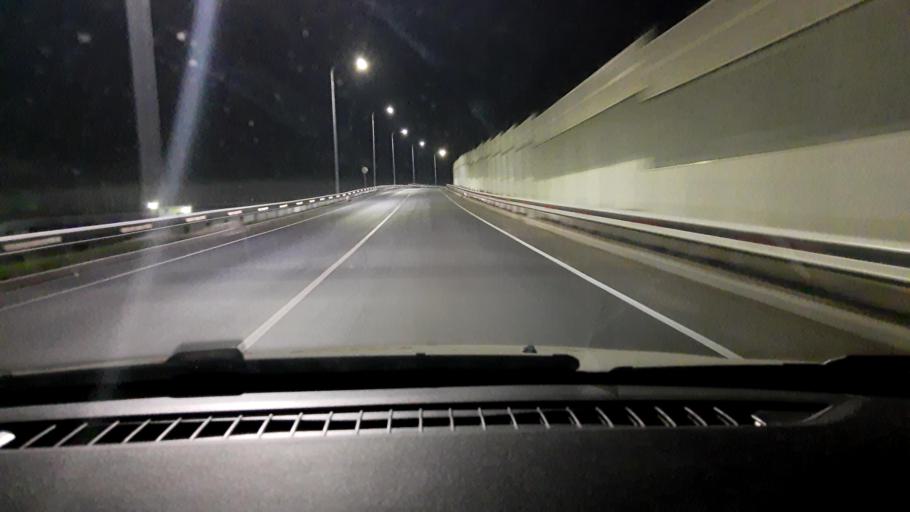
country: RU
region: Nizjnij Novgorod
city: Neklyudovo
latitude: 56.4147
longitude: 43.9835
